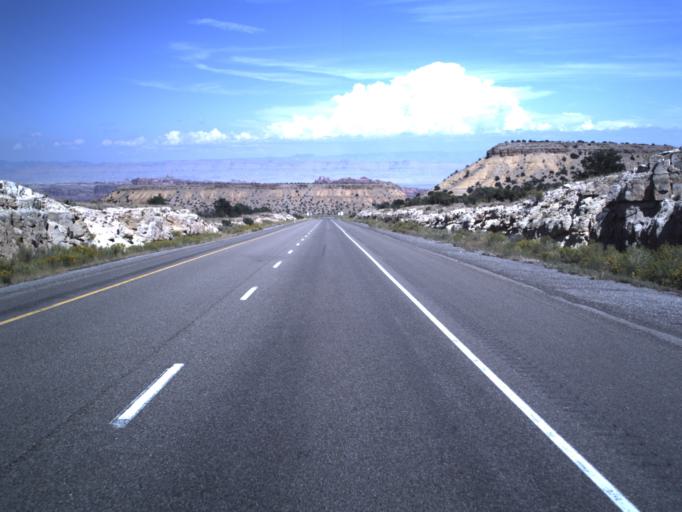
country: US
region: Utah
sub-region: Emery County
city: Castle Dale
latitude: 38.9087
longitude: -110.5280
